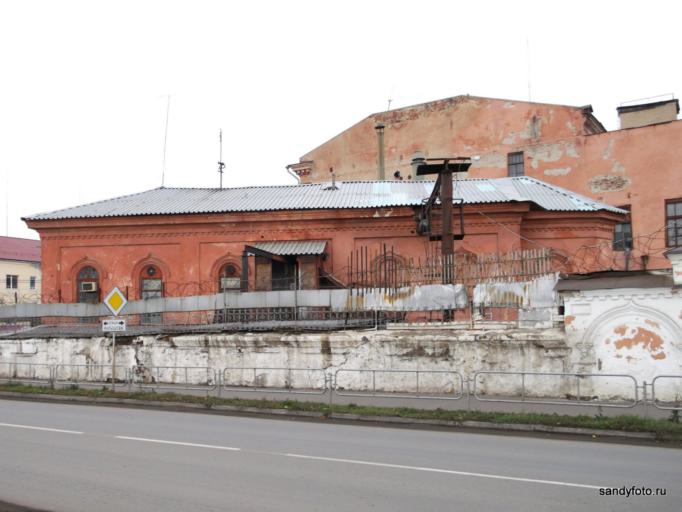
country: RU
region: Chelyabinsk
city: Troitsk
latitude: 54.0864
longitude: 61.5614
